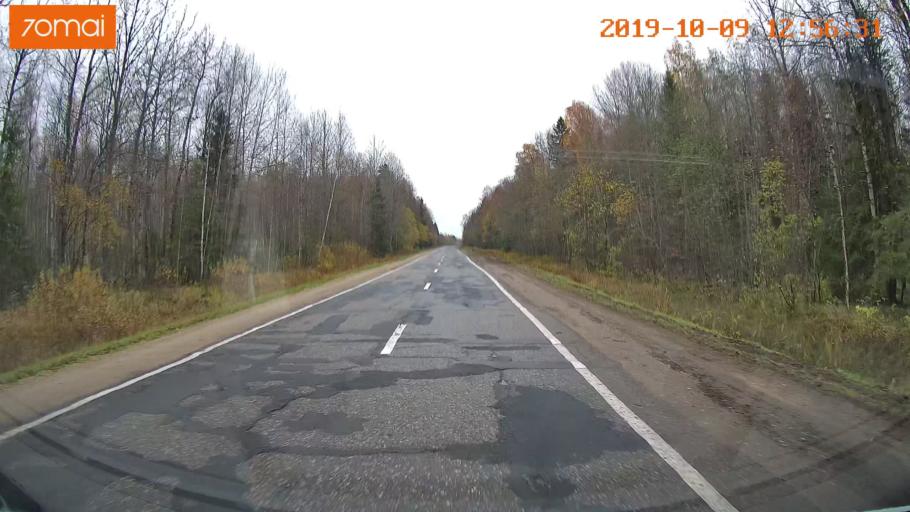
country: RU
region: Jaroslavl
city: Prechistoye
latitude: 58.3946
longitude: 40.4174
